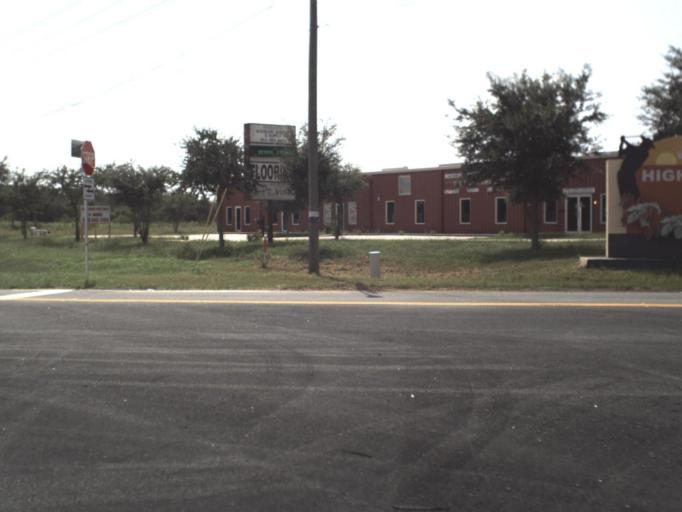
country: US
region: Florida
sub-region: Highlands County
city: Avon Park
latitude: 27.6467
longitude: -81.5305
